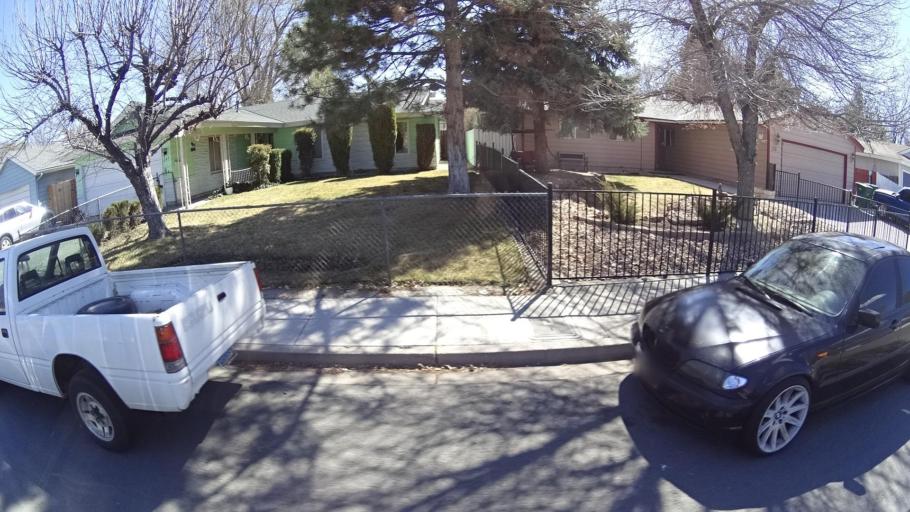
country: US
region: Nevada
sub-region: Washoe County
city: Sparks
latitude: 39.5386
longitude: -119.7405
